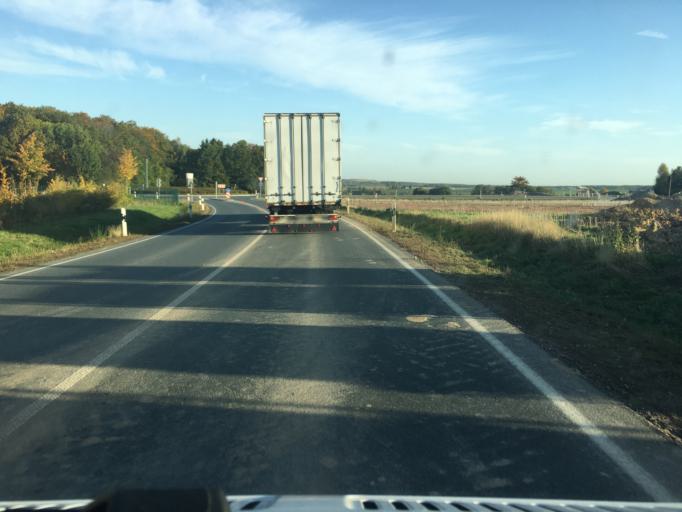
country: DE
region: Saxony
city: Hartmannsdorf
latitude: 50.7303
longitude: 12.4106
